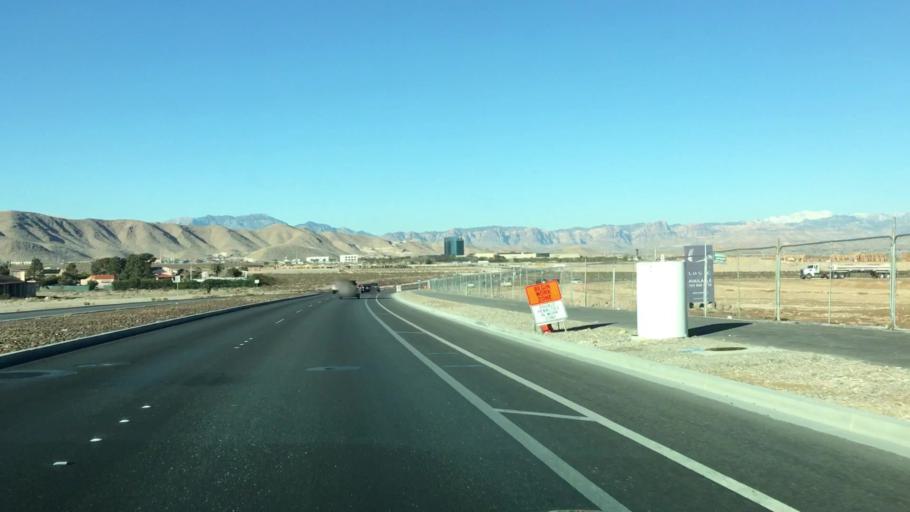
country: US
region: Nevada
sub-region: Clark County
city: Enterprise
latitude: 35.9602
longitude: -115.1480
